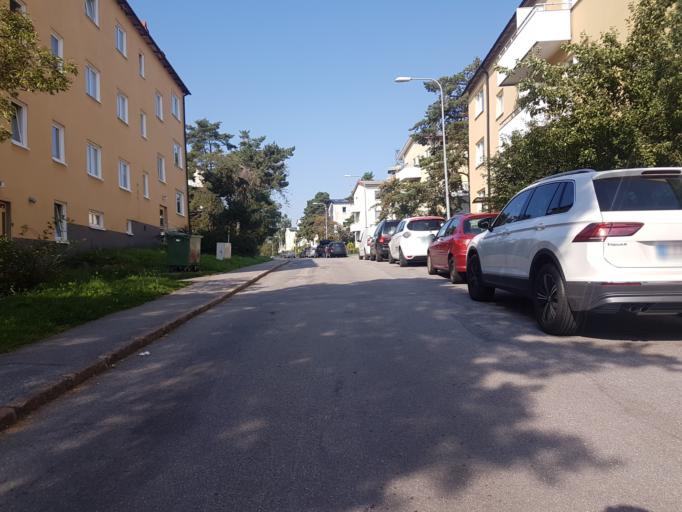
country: SE
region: Stockholm
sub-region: Stockholms Kommun
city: OEstermalm
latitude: 59.2975
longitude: 18.1030
